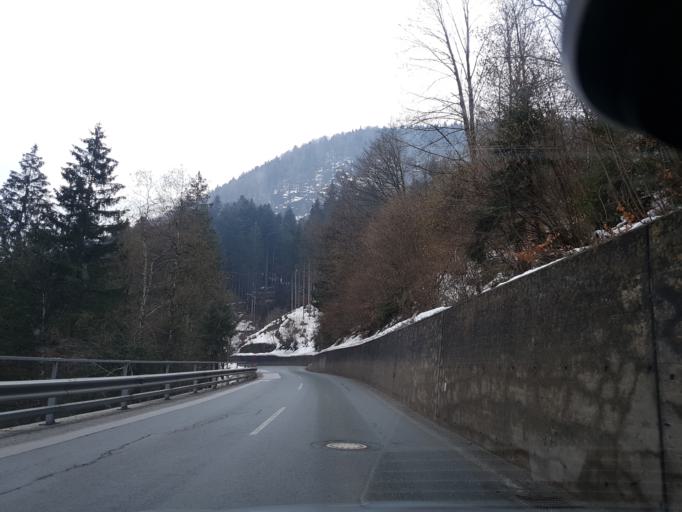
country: AT
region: Tyrol
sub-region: Politischer Bezirk Kufstein
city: Worgl
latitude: 47.4759
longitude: 12.0714
